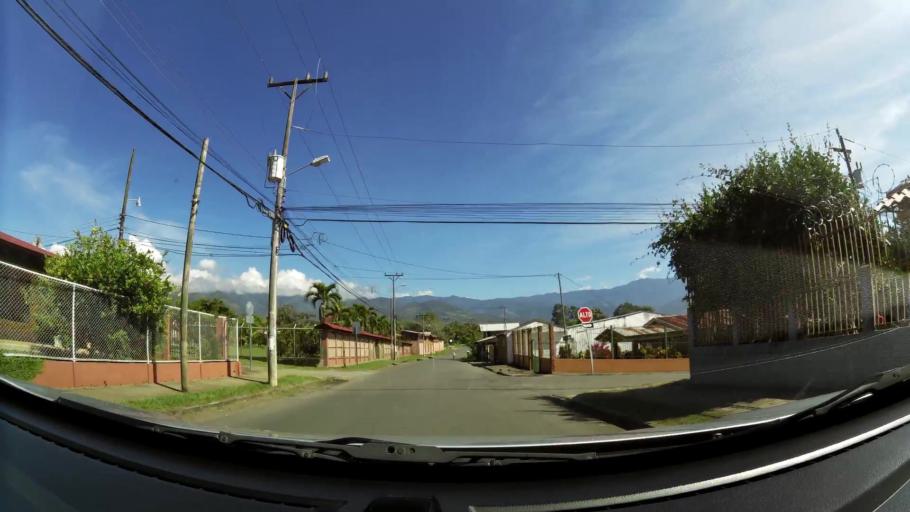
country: CR
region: San Jose
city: San Isidro
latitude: 9.3708
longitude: -83.7115
